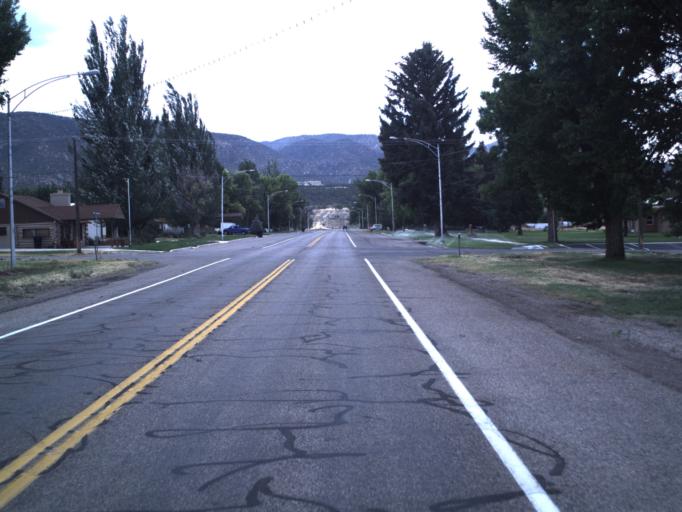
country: US
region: Utah
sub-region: Iron County
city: Parowan
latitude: 37.8879
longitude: -112.7751
